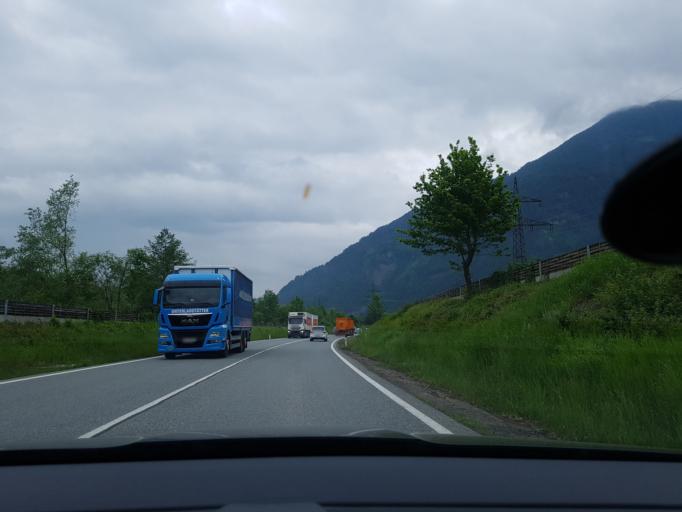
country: AT
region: Tyrol
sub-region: Politischer Bezirk Schwaz
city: Ried im Zillertal
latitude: 47.2951
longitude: 11.8763
